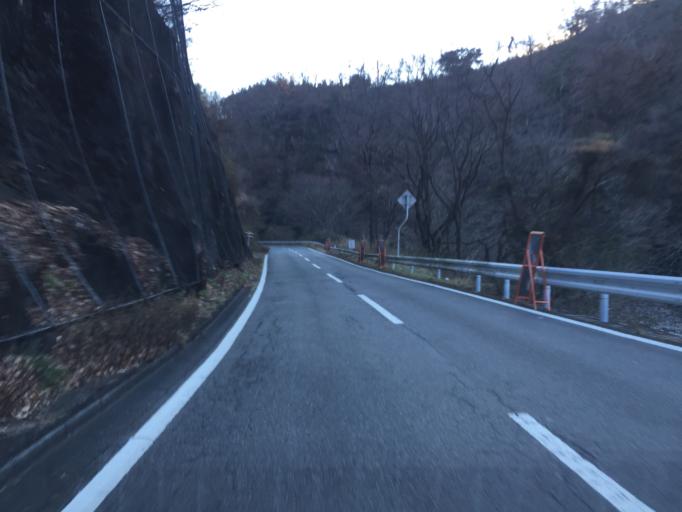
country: JP
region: Fukushima
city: Iwaki
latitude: 37.1554
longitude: 140.8271
